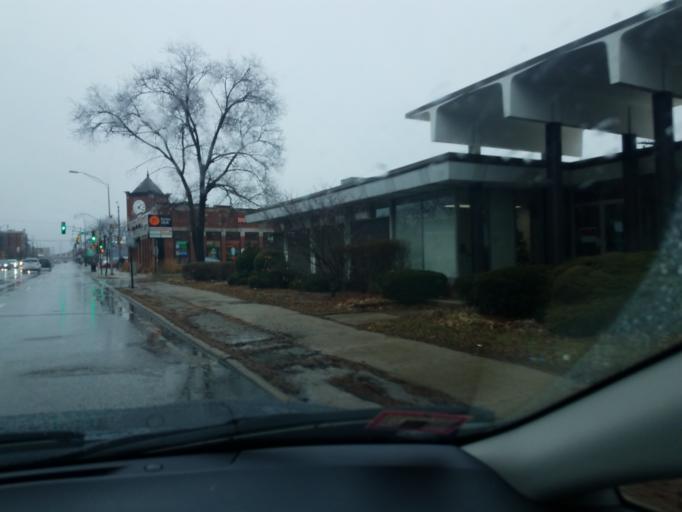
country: US
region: Illinois
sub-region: Cook County
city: Skokie
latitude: 42.0343
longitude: -87.7474
